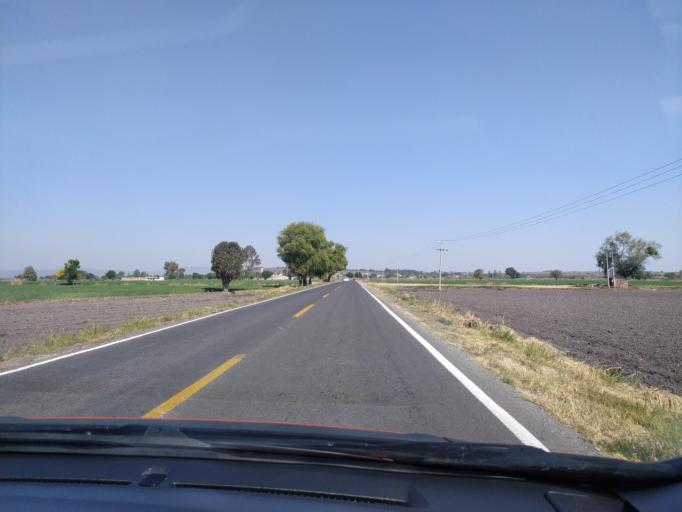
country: MX
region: Guanajuato
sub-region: San Francisco del Rincon
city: San Ignacio de Hidalgo
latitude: 20.8422
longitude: -101.8476
